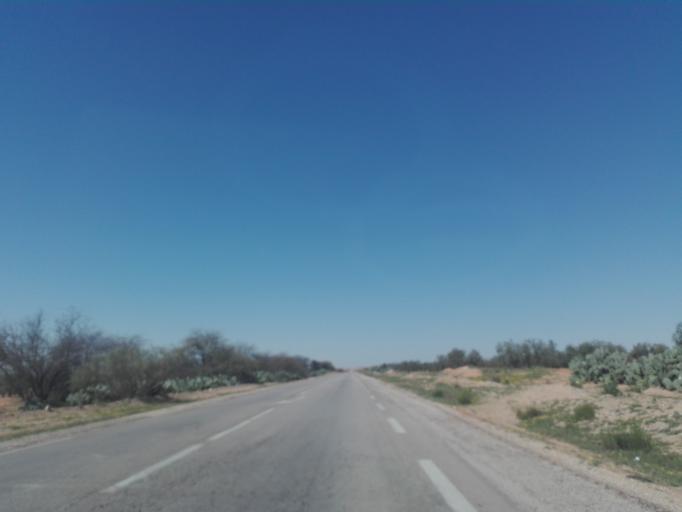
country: TN
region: Safaqis
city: Bi'r `Ali Bin Khalifah
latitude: 34.7572
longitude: 10.2681
